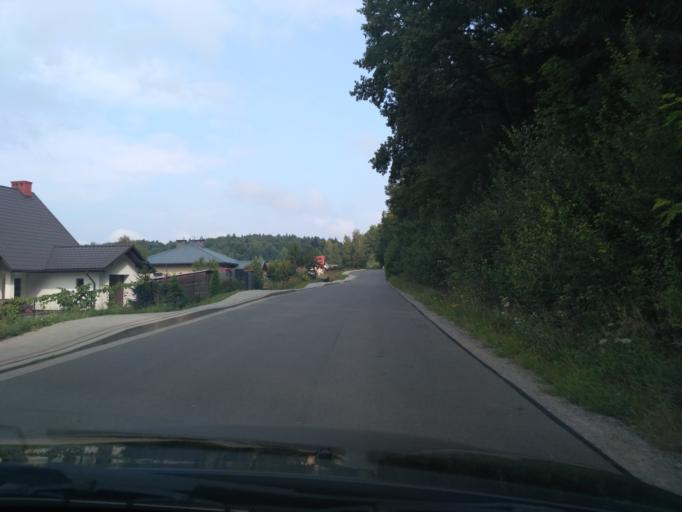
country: PL
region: Subcarpathian Voivodeship
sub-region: Powiat strzyzowski
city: Czudec
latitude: 49.9613
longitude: 21.8441
